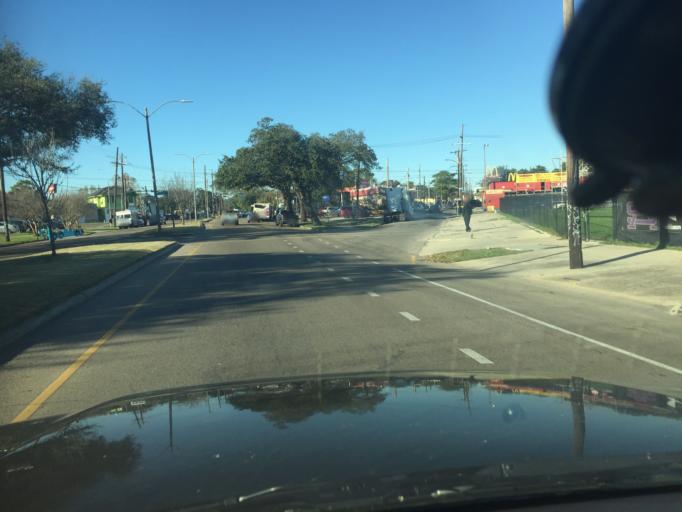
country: US
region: Louisiana
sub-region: Orleans Parish
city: New Orleans
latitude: 29.9822
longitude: -90.0711
